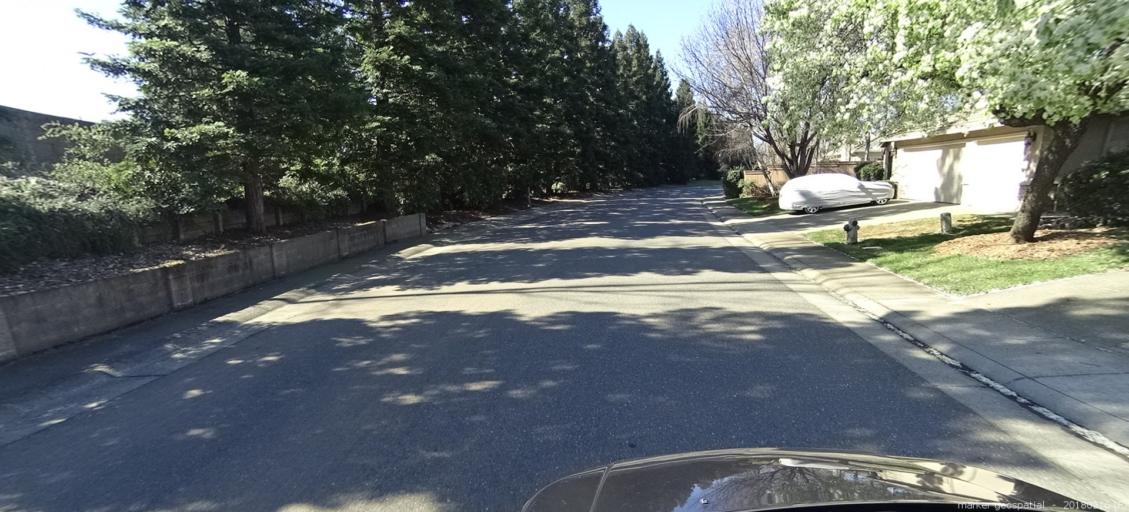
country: US
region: California
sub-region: Sacramento County
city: Gold River
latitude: 38.6209
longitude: -121.2401
